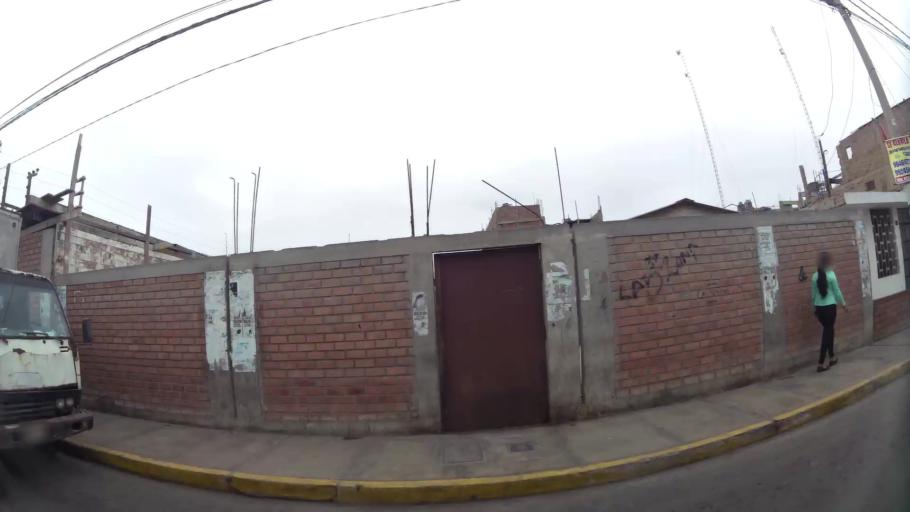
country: PE
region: Ica
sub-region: Provincia de Pisco
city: Pisco
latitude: -13.7115
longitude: -76.2029
